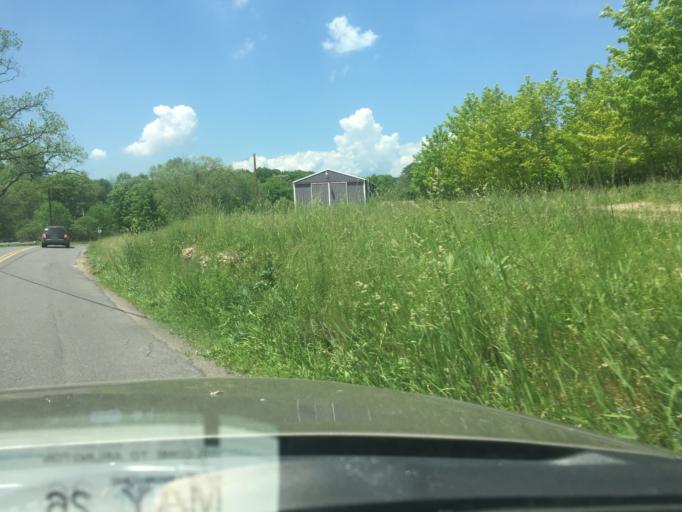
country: US
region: Pennsylvania
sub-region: Luzerne County
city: Conyngham
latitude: 41.0282
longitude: -76.0148
